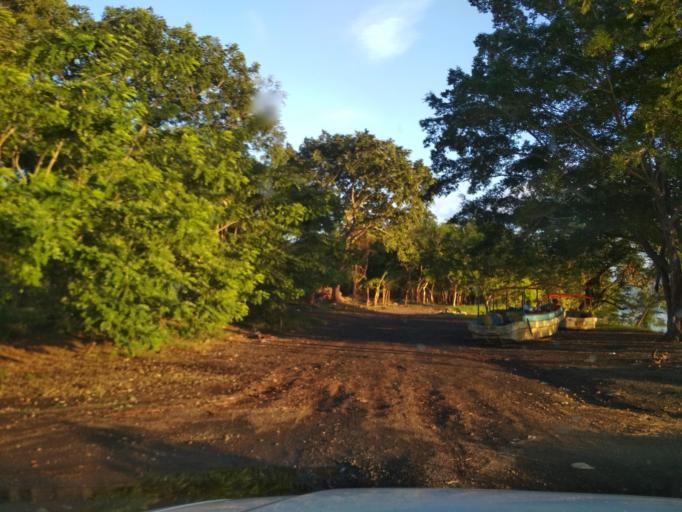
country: MX
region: Veracruz
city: Catemaco
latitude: 18.4165
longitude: -95.1051
